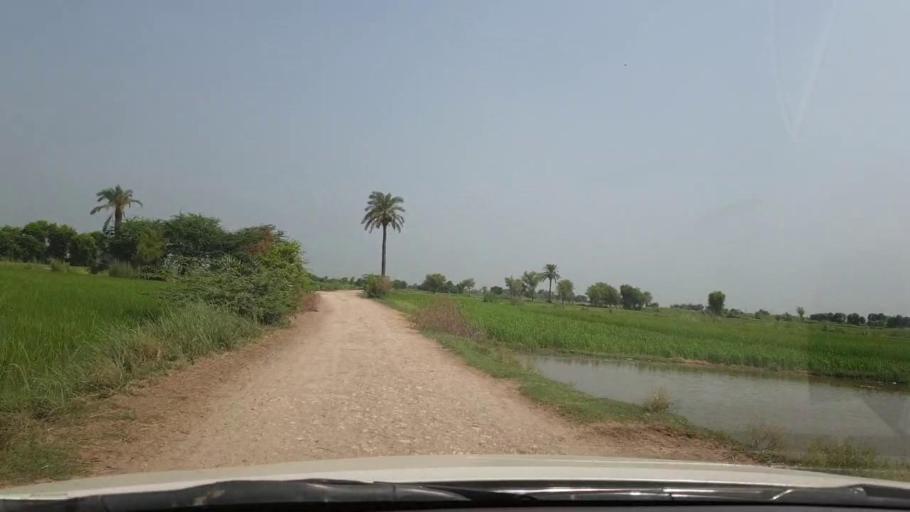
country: PK
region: Sindh
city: Shikarpur
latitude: 27.9600
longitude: 68.7078
